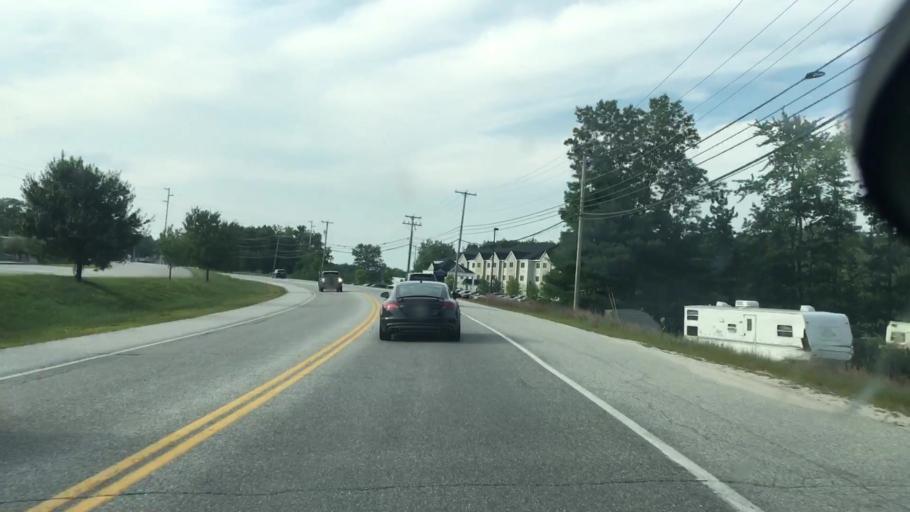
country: US
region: Maine
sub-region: Cumberland County
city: North Windham
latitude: 43.8555
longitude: -70.4515
